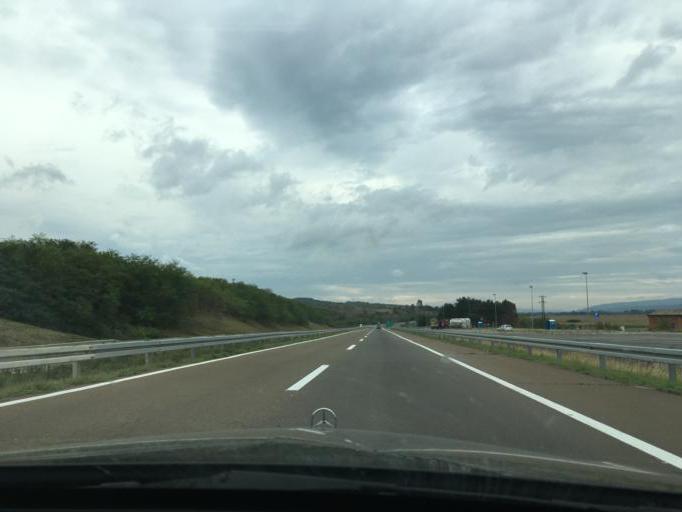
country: RS
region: Central Serbia
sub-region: Nisavski Okrug
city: Aleksinac
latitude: 43.5744
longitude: 21.6706
